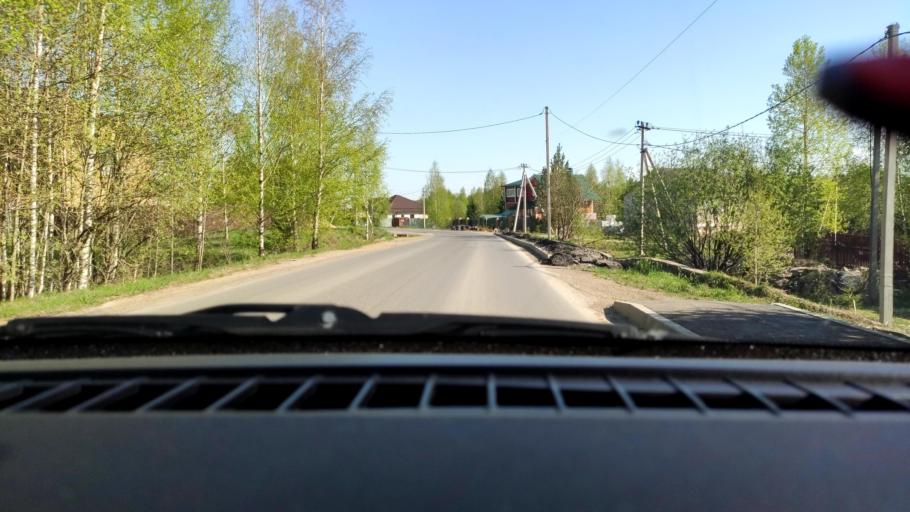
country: RU
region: Perm
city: Kondratovo
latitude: 58.0588
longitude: 56.0054
